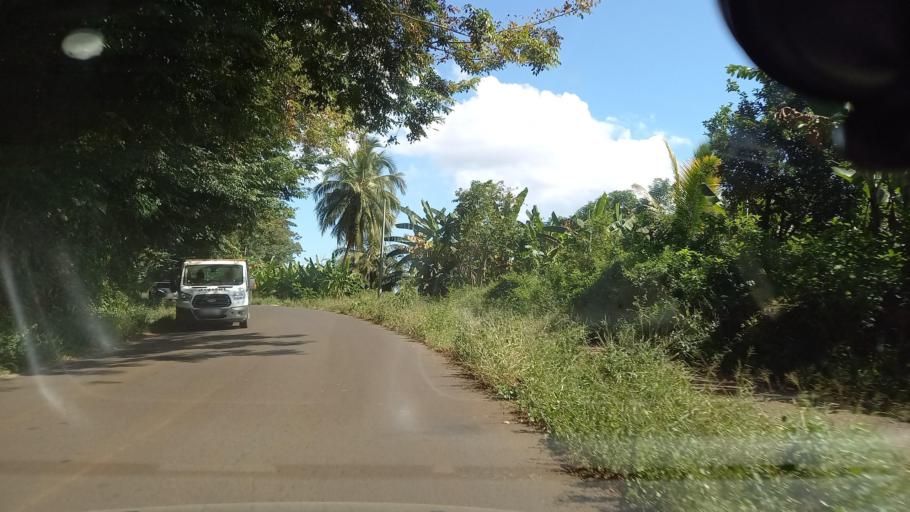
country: YT
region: Tsingoni
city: Tsingoni
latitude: -12.7928
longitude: 45.1205
